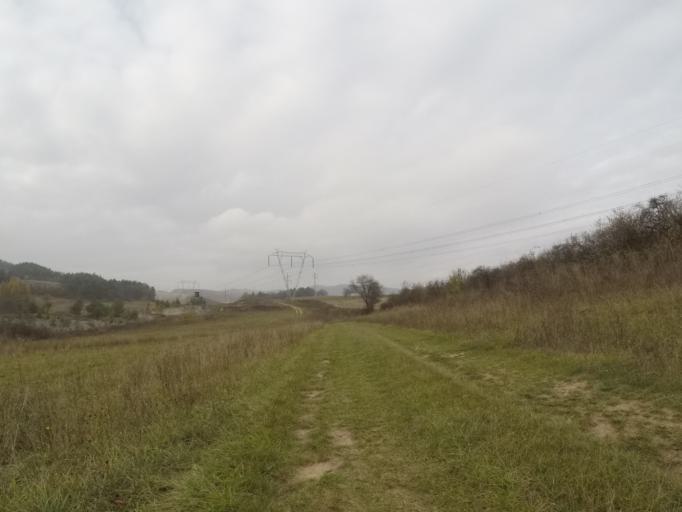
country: SK
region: Presovsky
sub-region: Okres Presov
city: Presov
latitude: 48.9040
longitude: 21.1811
